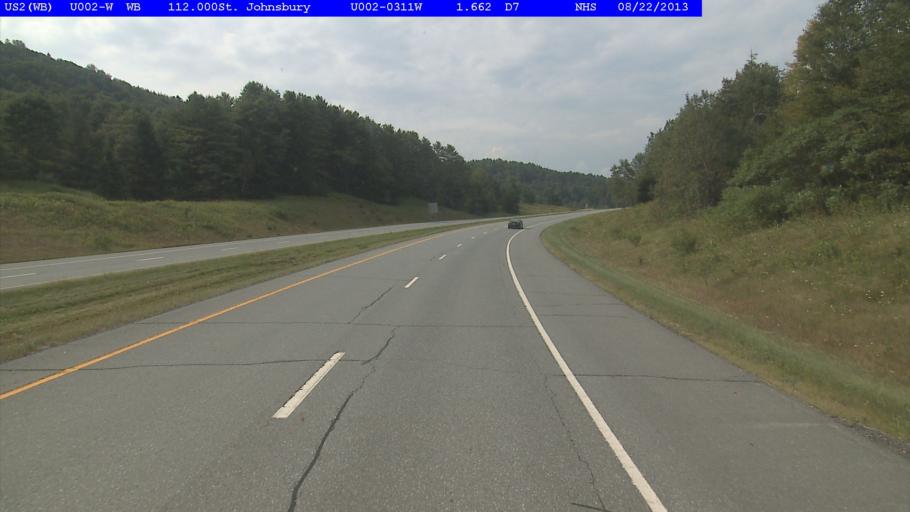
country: US
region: Vermont
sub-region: Caledonia County
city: St Johnsbury
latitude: 44.4312
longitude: -72.0392
